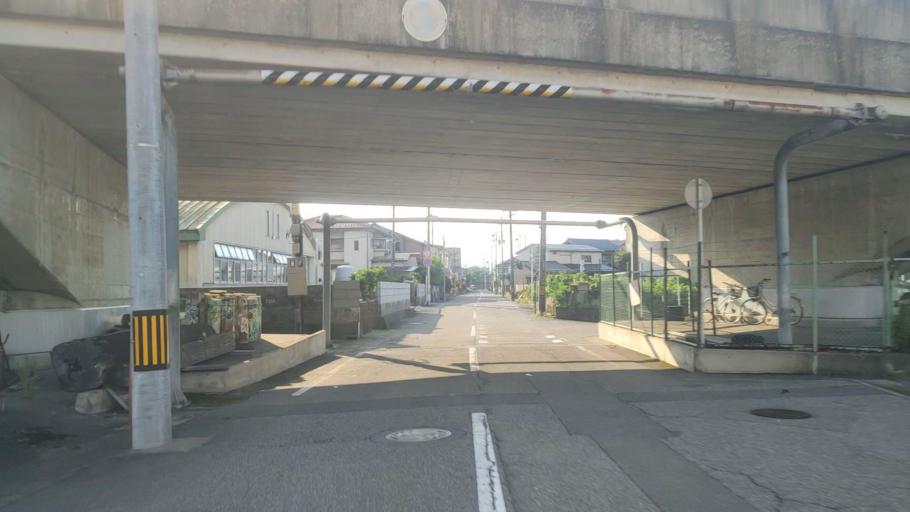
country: JP
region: Fukui
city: Fukui-shi
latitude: 36.0507
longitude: 136.2340
